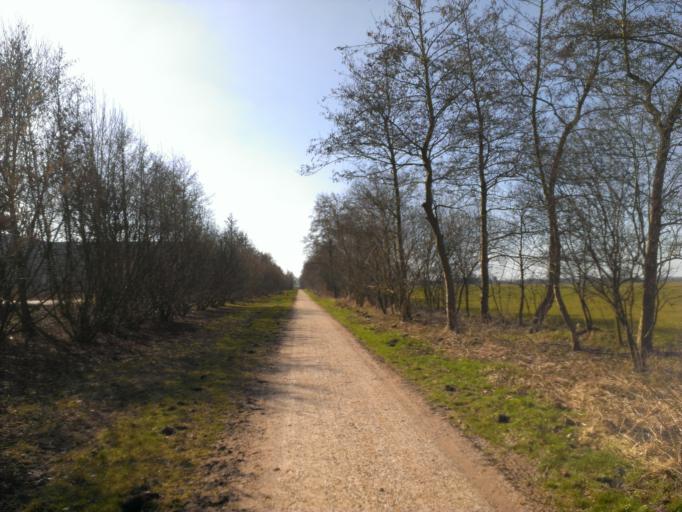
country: NL
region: Gelderland
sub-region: Gemeente Voorst
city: Twello
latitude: 52.2285
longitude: 6.0860
